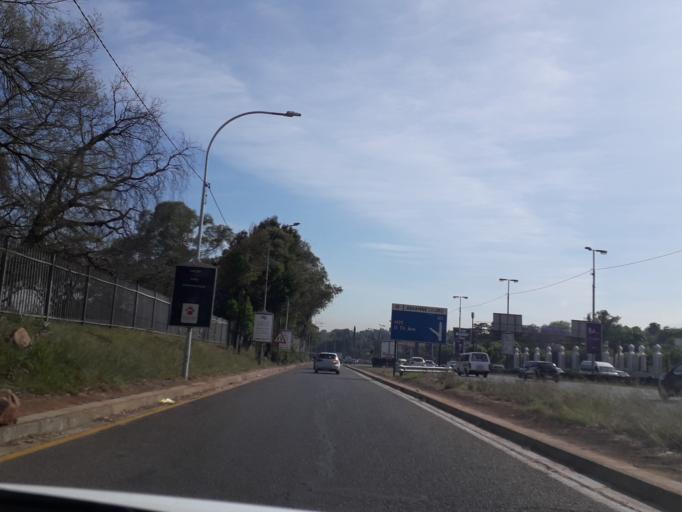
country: ZA
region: Gauteng
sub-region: City of Johannesburg Metropolitan Municipality
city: Johannesburg
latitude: -26.1636
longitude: 28.0561
